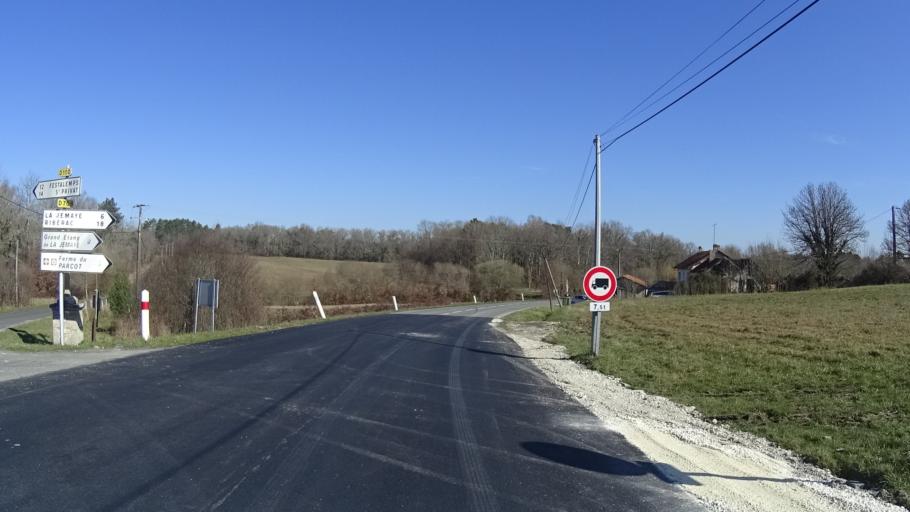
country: FR
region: Aquitaine
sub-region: Departement de la Dordogne
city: Saint-Aulaye
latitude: 45.1280
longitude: 0.2300
